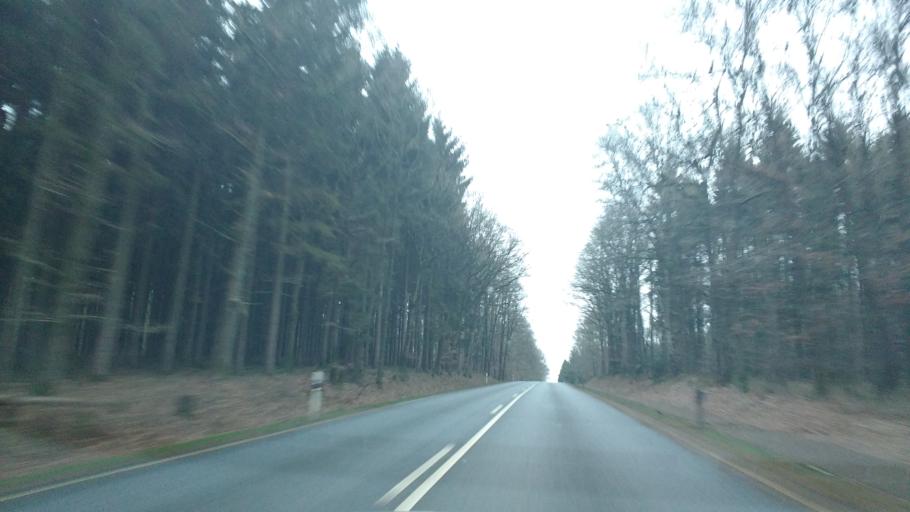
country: DE
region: Schleswig-Holstein
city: Silzen
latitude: 54.0413
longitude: 9.6138
